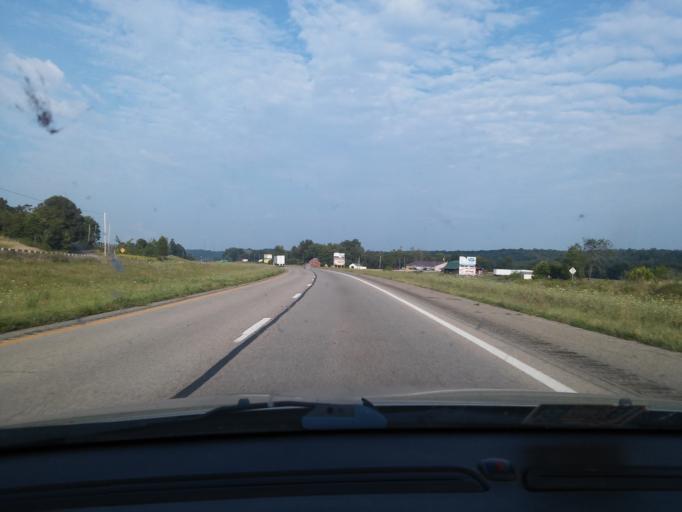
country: US
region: Ohio
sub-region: Jackson County
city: Oak Hill
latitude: 38.8843
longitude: -82.4199
